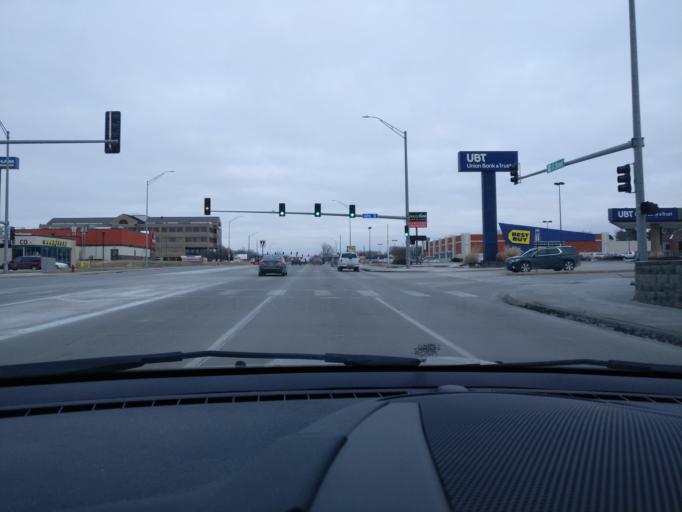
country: US
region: Nebraska
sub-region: Lancaster County
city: Lincoln
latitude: 40.8133
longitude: -96.6283
